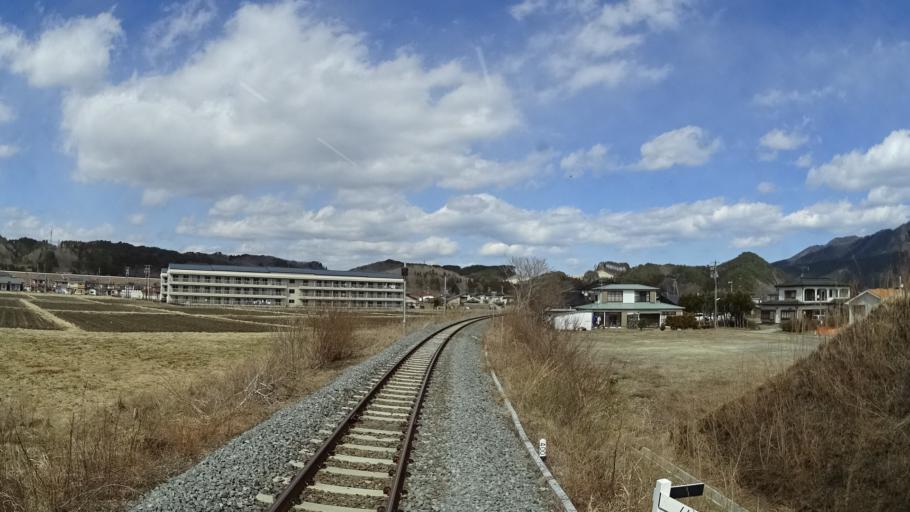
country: JP
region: Iwate
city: Yamada
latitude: 39.5383
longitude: 141.9255
